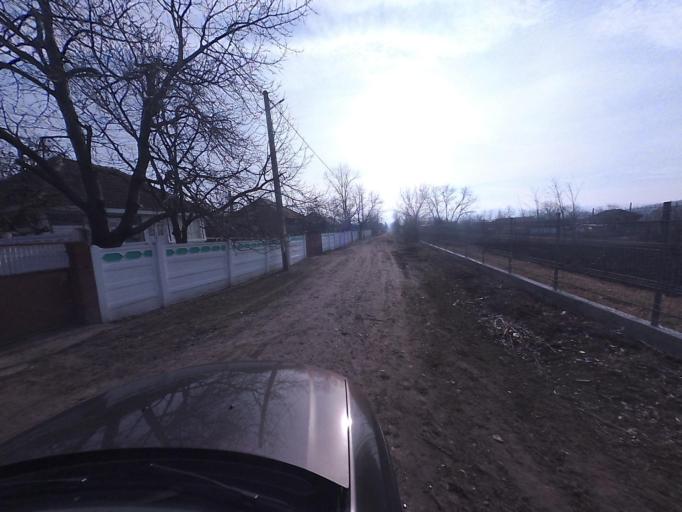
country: RO
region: Vaslui
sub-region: Comuna Solesti
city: Solesti
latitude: 46.8086
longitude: 27.7815
